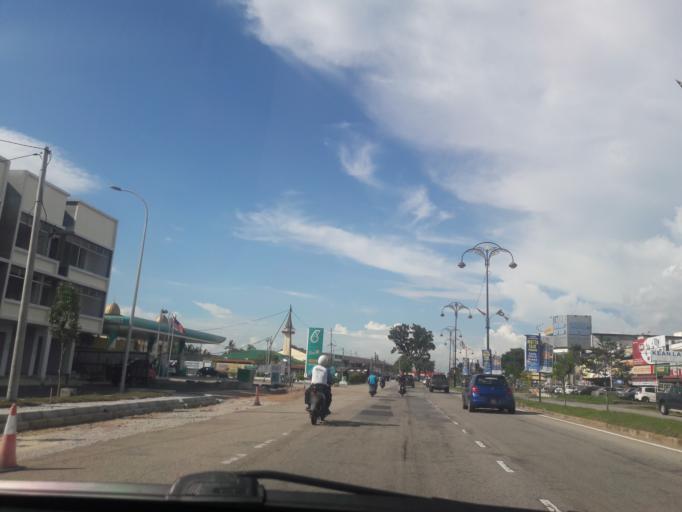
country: MY
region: Kedah
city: Sungai Petani
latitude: 5.6281
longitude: 100.4801
